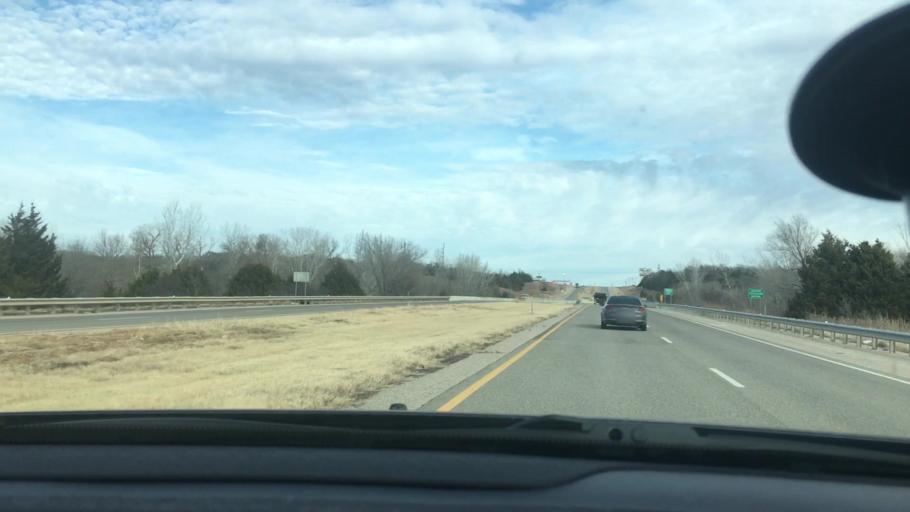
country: US
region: Oklahoma
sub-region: Pontotoc County
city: Byng
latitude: 34.9300
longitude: -96.6836
